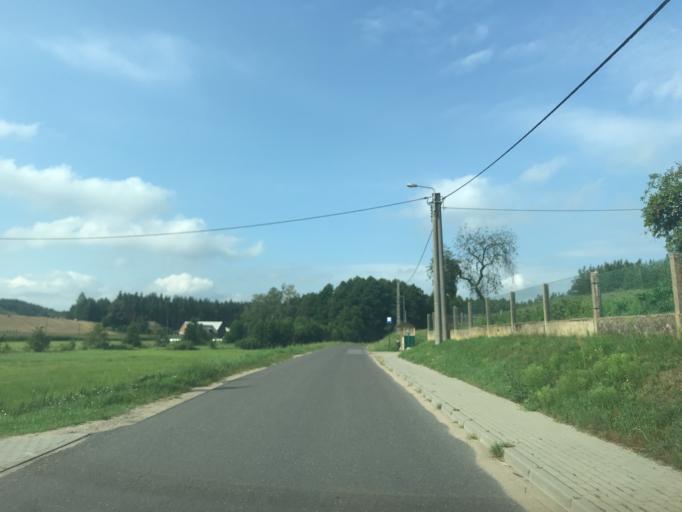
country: PL
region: Warmian-Masurian Voivodeship
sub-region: Powiat nowomiejski
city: Kurzetnik
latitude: 53.3715
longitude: 19.5489
